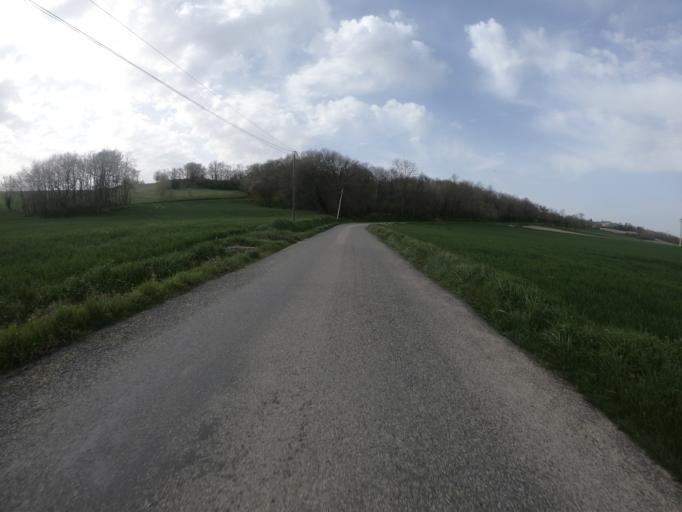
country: FR
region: Midi-Pyrenees
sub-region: Departement de l'Ariege
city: La Tour-du-Crieu
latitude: 43.1342
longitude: 1.7136
